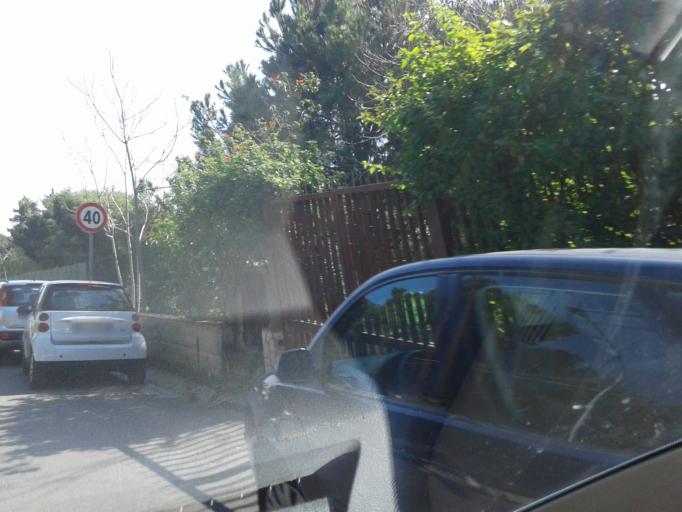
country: IT
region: Sicily
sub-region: Palermo
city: Piano dei Geli
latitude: 38.1184
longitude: 13.2978
